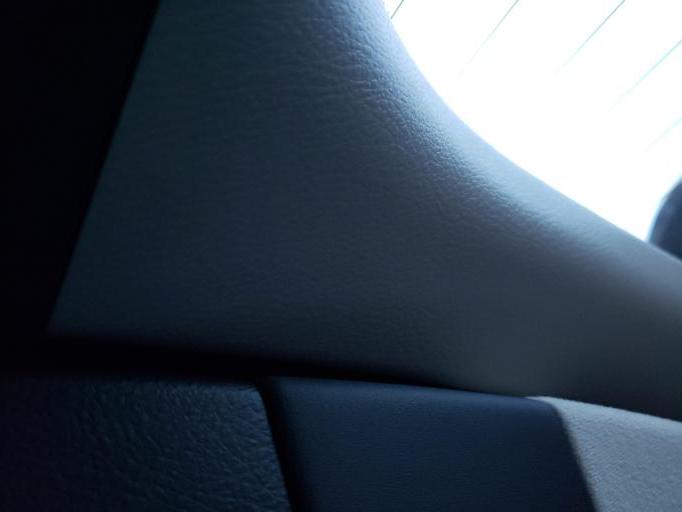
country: JP
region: Ehime
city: Hojo
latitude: 34.0420
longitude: 132.9760
